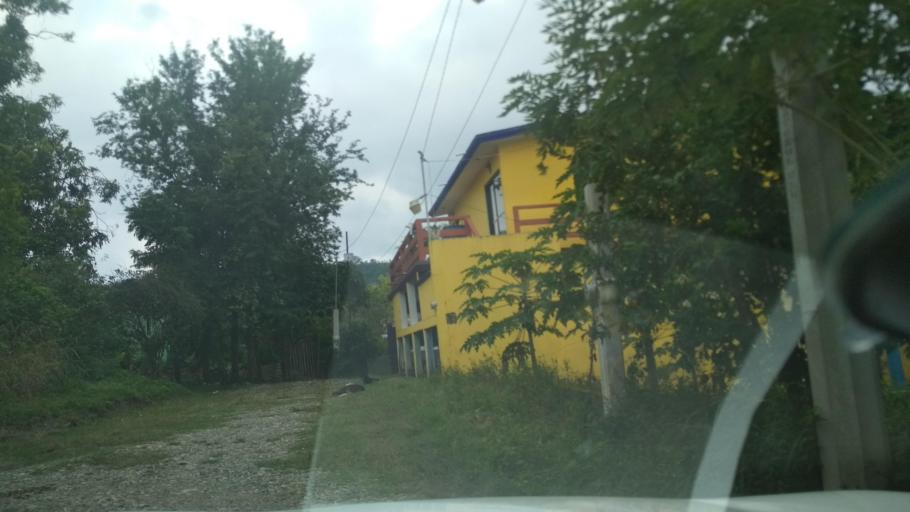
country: MX
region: Veracruz
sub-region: Poza Rica de Hidalgo
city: Arroyo del Maiz Uno
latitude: 20.5153
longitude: -97.3812
